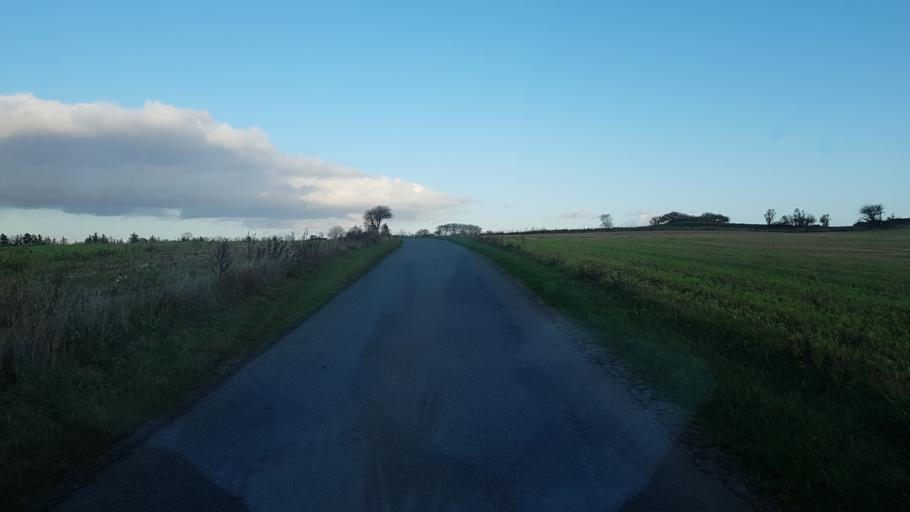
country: DK
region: South Denmark
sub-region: Vejen Kommune
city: Brorup
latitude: 55.4548
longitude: 8.9655
